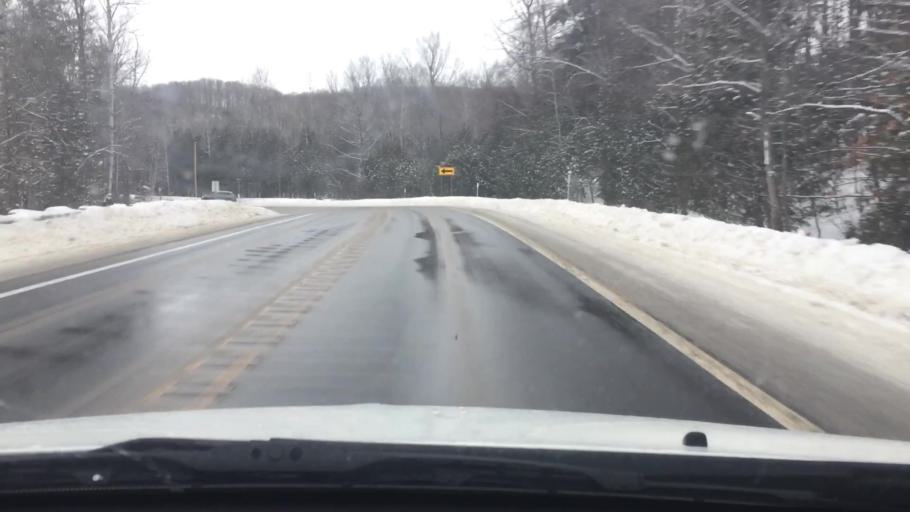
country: US
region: Michigan
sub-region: Charlevoix County
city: East Jordan
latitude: 45.1313
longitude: -85.0812
